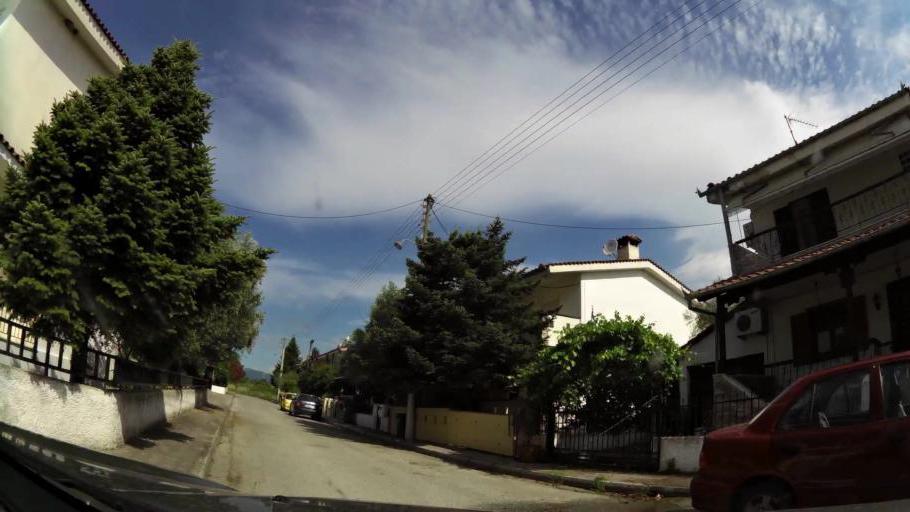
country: GR
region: Central Macedonia
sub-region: Nomos Pierias
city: Katerini
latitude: 40.2851
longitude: 22.5177
